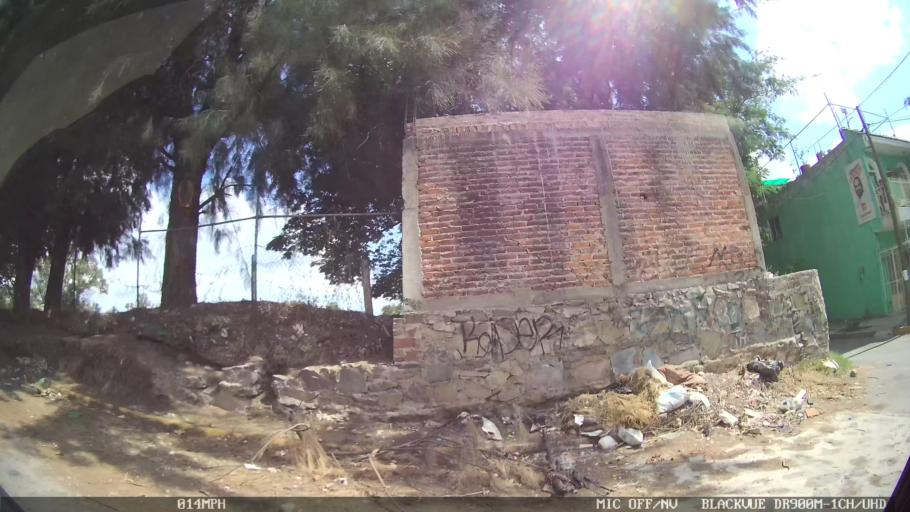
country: MX
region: Jalisco
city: Tlaquepaque
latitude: 20.6260
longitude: -103.2688
